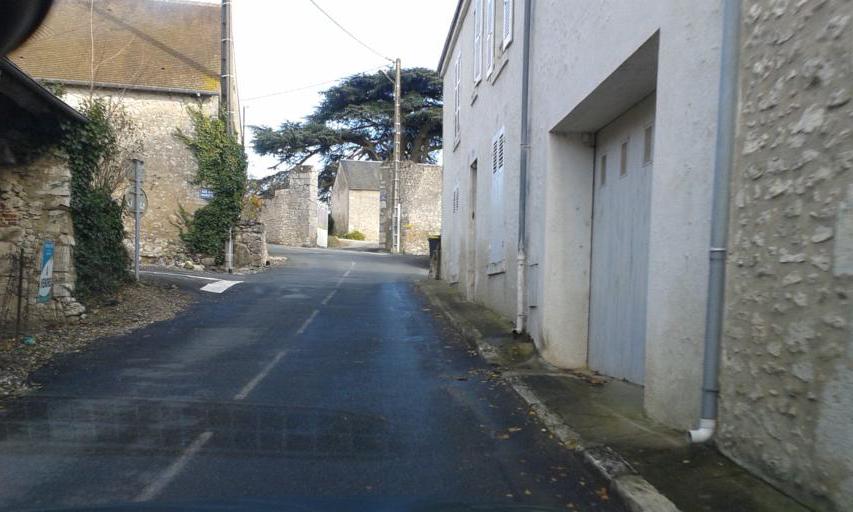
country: FR
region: Centre
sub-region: Departement du Loiret
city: Tavers
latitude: 47.7558
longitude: 1.6145
